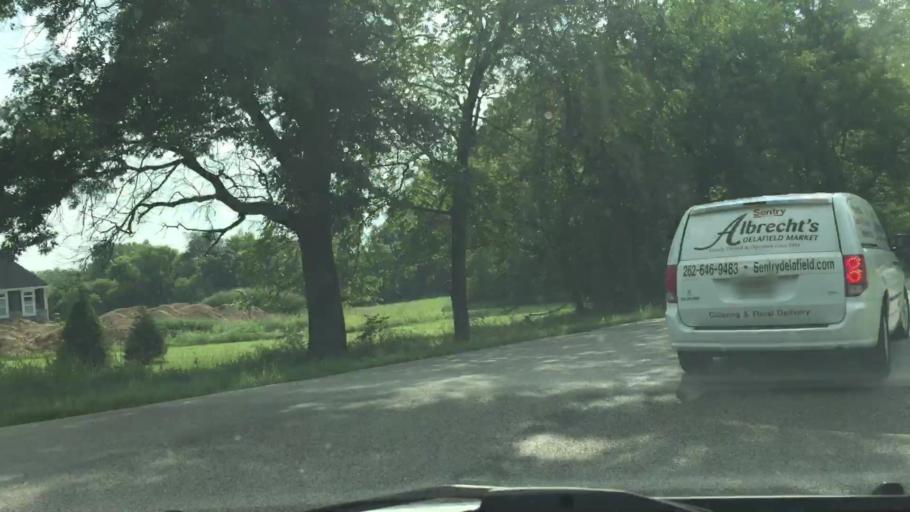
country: US
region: Wisconsin
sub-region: Waukesha County
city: Wales
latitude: 43.0407
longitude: -88.3497
